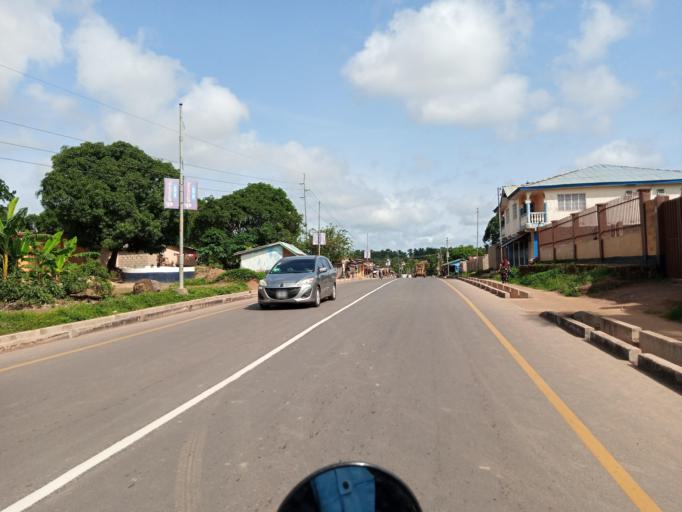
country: SL
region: Southern Province
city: Bo
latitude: 7.9503
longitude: -11.7155
